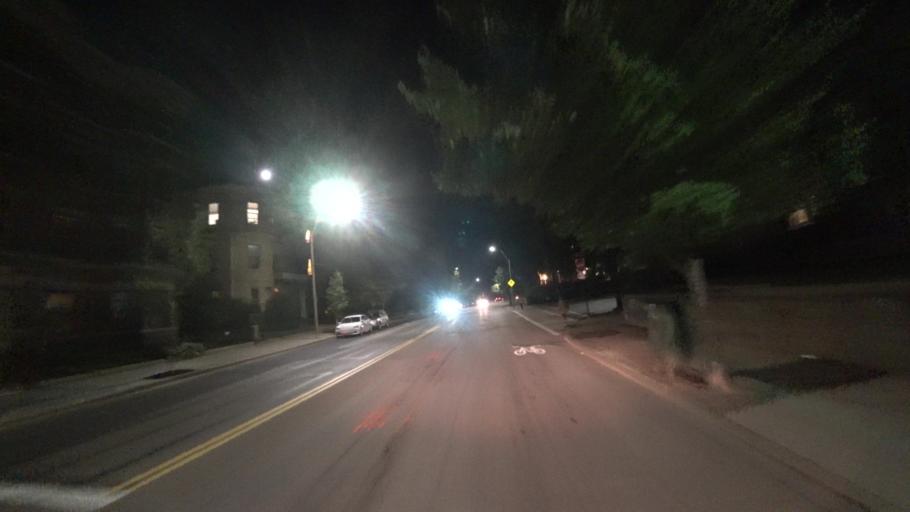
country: US
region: Massachusetts
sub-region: Norfolk County
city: Brookline
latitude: 42.3364
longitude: -71.1259
